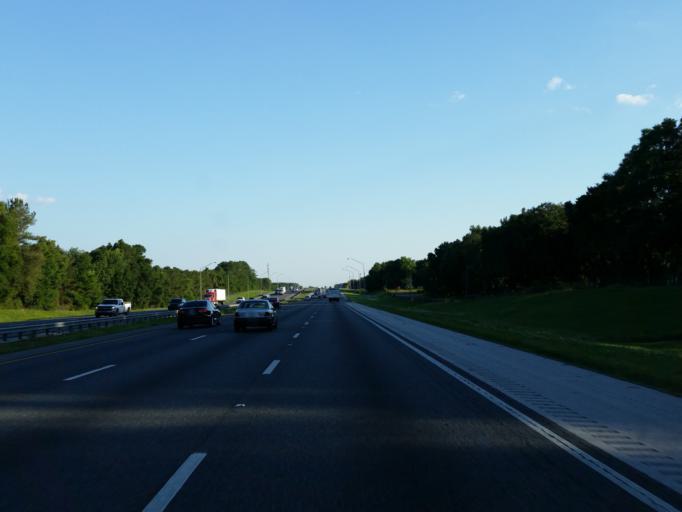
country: US
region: Florida
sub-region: Marion County
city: Ocala
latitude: 29.1027
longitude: -82.1851
